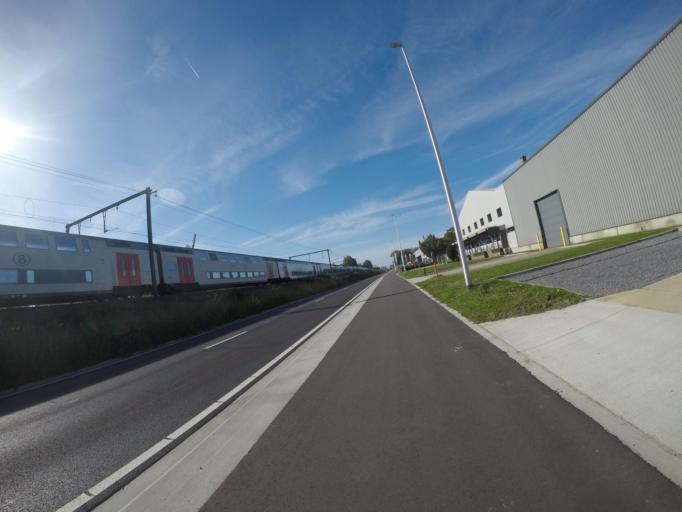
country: BE
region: Flanders
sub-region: Provincie Limburg
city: Diepenbeek
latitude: 50.9094
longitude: 5.4246
